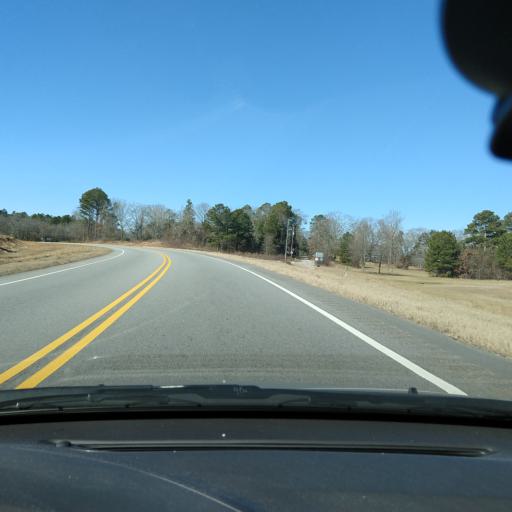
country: US
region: Georgia
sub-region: Walton County
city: Social Circle
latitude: 33.6407
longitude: -83.7198
